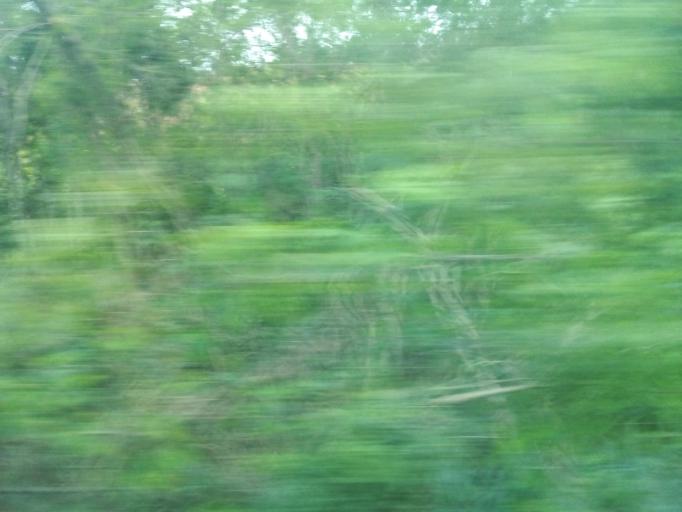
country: BR
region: Minas Gerais
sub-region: Ipaba
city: Ipaba
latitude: -19.4617
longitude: -42.4604
